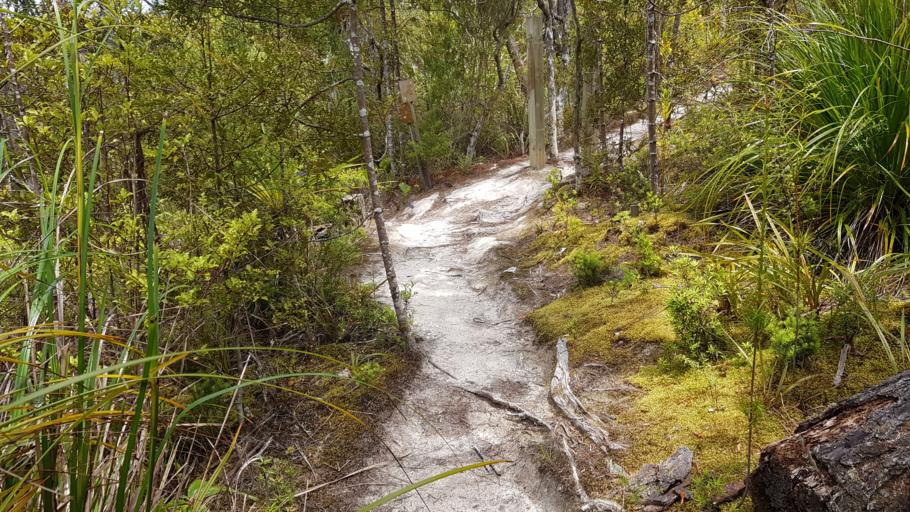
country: NZ
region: Auckland
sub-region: Auckland
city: North Shore
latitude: -36.8238
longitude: 174.7059
